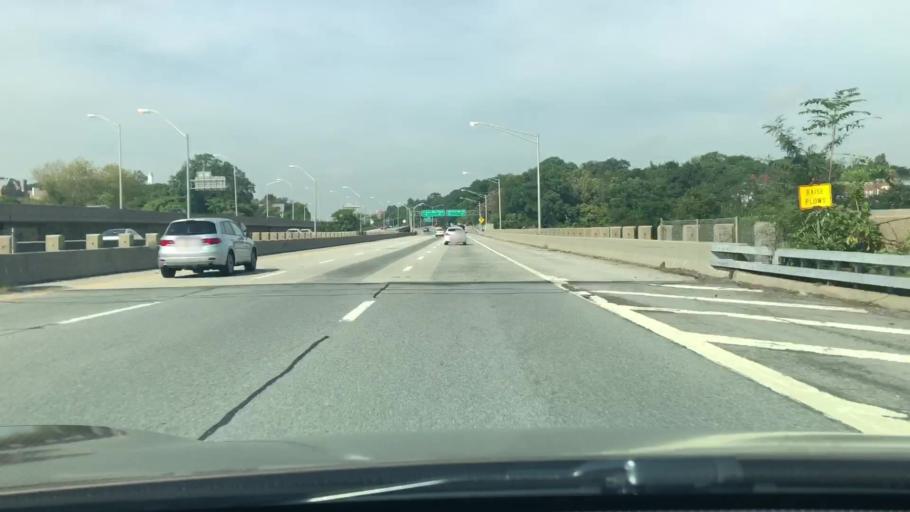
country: US
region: New York
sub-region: Westchester County
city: Bronxville
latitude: 40.9275
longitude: -73.8387
